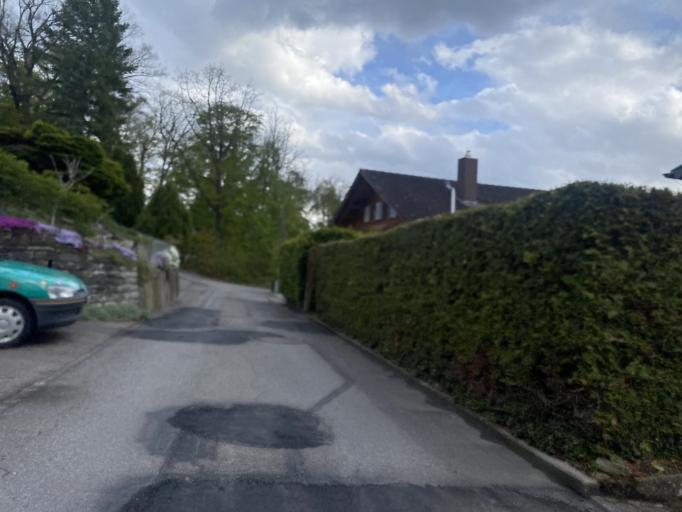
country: CH
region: Bern
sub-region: Thun District
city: Hilterfingen
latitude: 46.7418
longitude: 7.6552
